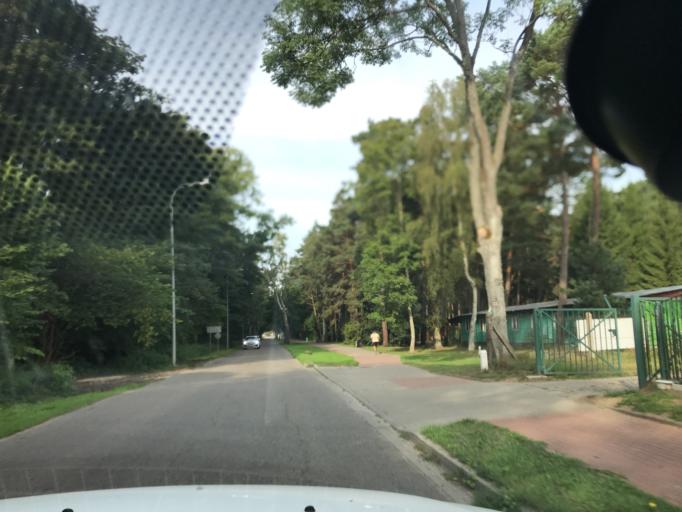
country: PL
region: West Pomeranian Voivodeship
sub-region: Powiat slawienski
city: Darlowo
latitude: 54.5391
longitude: 16.5615
